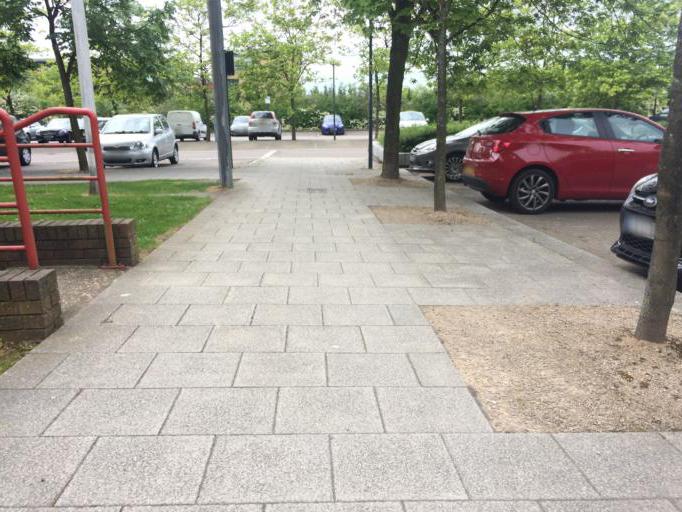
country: GB
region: England
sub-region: Milton Keynes
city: Milton Keynes
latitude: 52.0416
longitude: -0.7672
